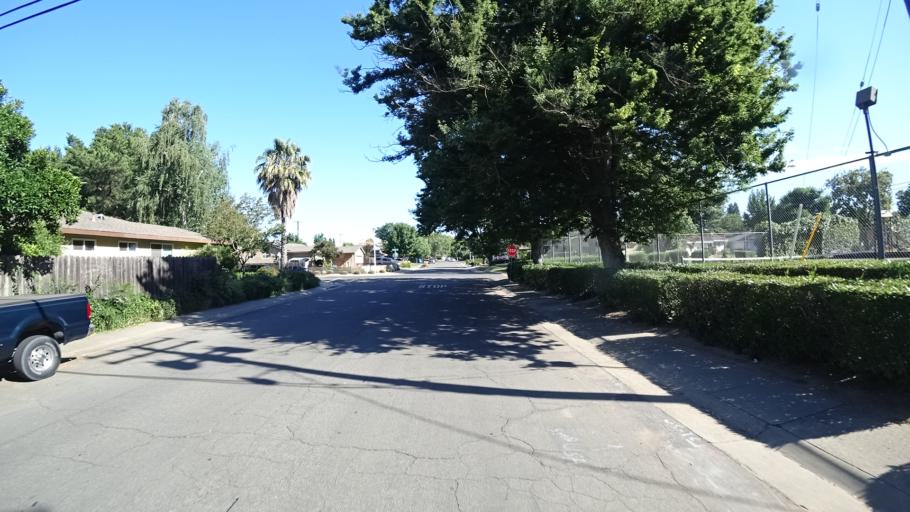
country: US
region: California
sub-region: Sacramento County
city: Rosemont
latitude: 38.5533
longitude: -121.3970
